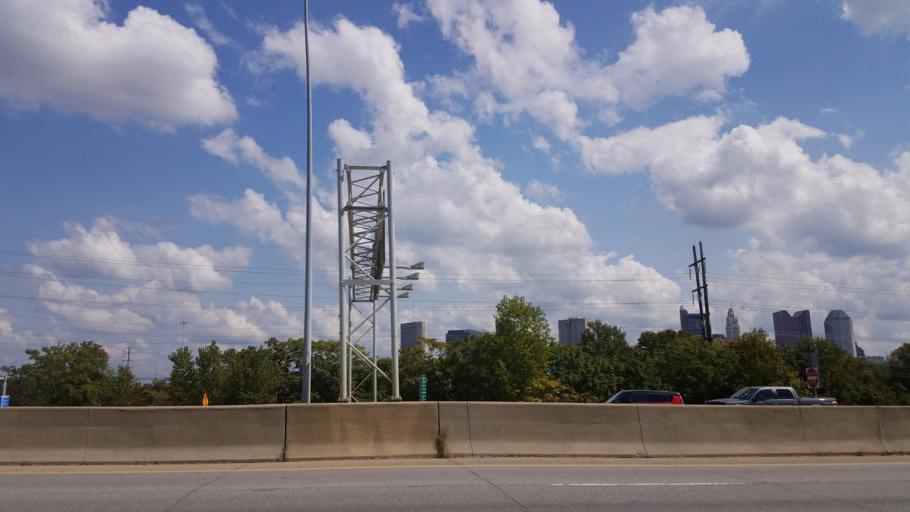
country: US
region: Ohio
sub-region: Franklin County
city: Columbus
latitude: 39.9645
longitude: -83.0205
